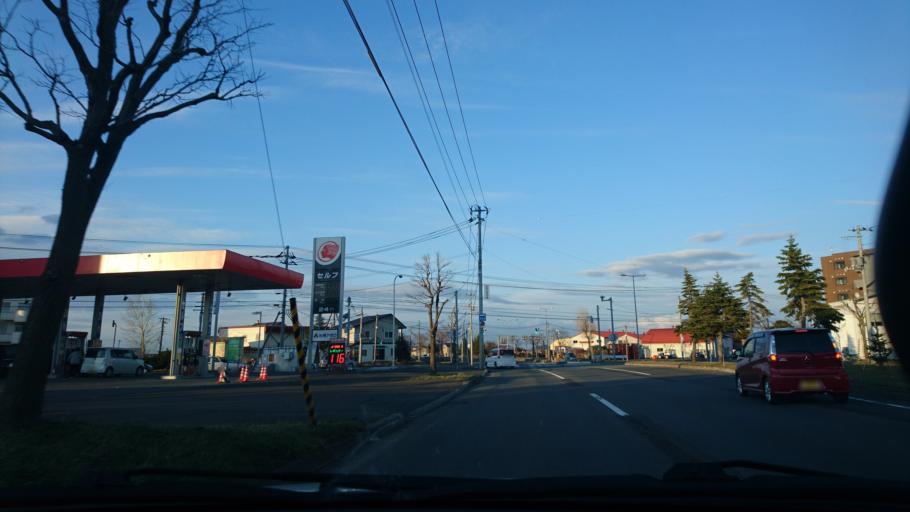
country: JP
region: Hokkaido
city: Sapporo
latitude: 43.1040
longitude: 141.3934
